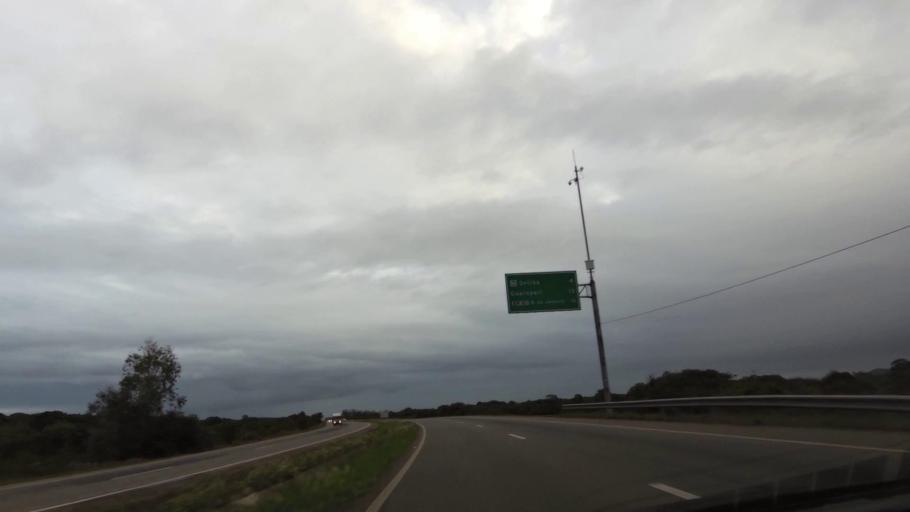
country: BR
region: Espirito Santo
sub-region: Guarapari
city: Guarapari
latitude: -20.5874
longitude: -40.4244
